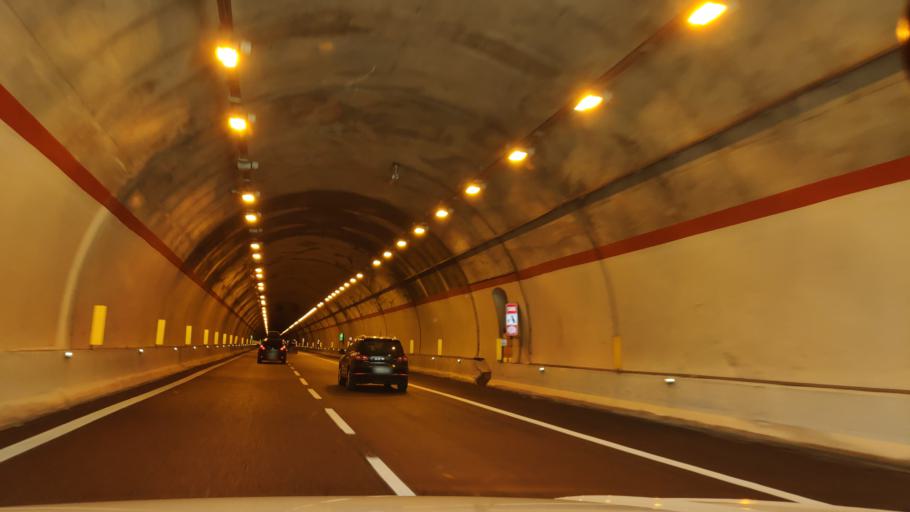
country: IT
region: Calabria
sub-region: Provincia di Cosenza
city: Morano Calabro
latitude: 39.8771
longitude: 16.1270
